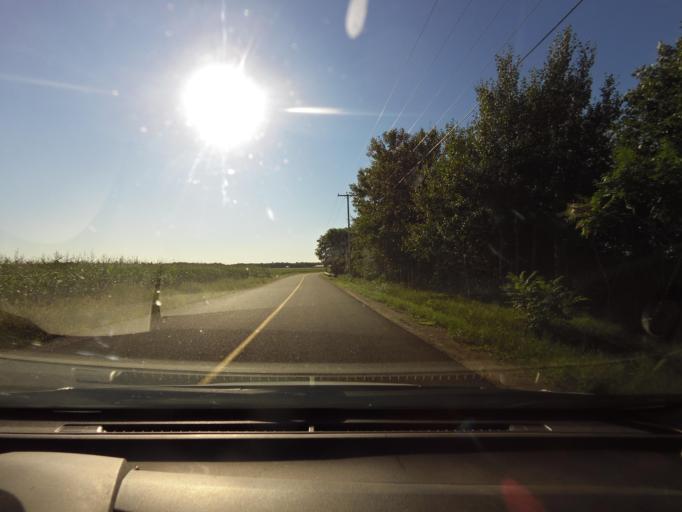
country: CA
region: Quebec
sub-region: Mauricie
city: Becancour
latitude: 46.5541
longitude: -72.3632
